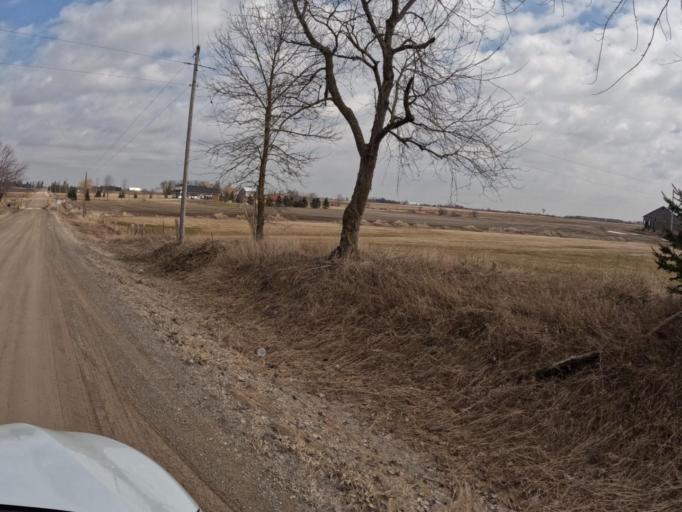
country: CA
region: Ontario
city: Orangeville
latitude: 43.9043
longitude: -80.2361
